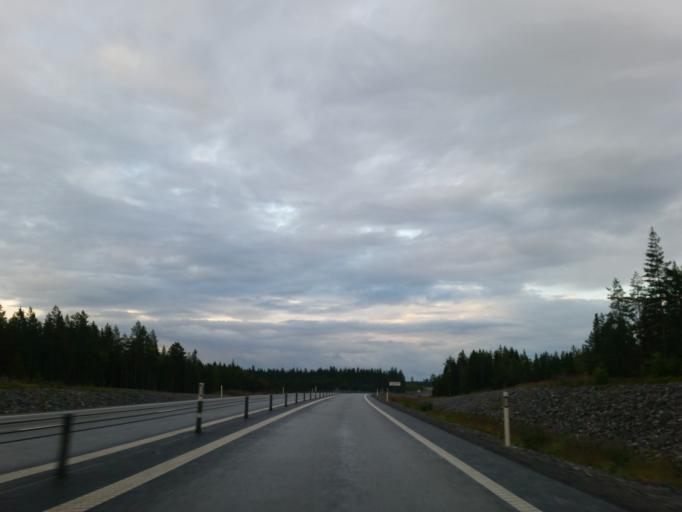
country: SE
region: Vaesterbotten
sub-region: Umea Kommun
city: Umea
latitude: 63.8580
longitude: 20.2450
